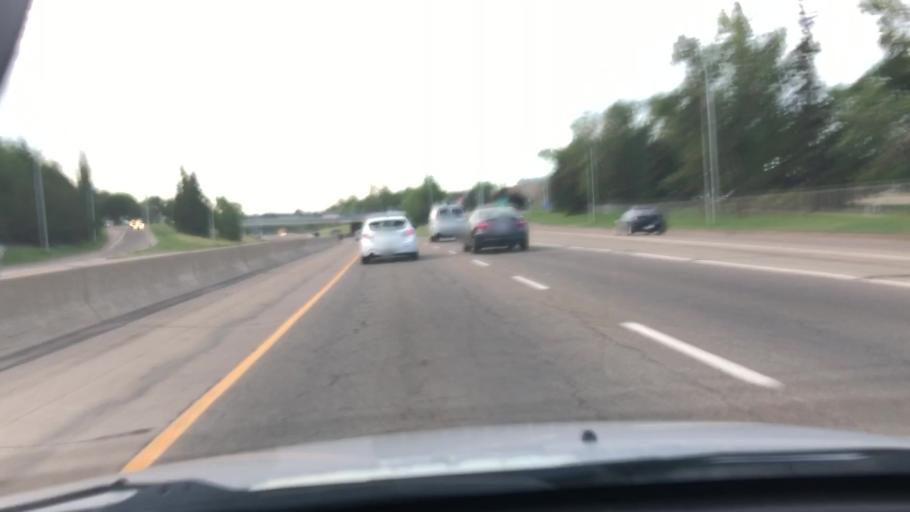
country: CA
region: Alberta
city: Edmonton
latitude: 53.5650
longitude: -113.4490
